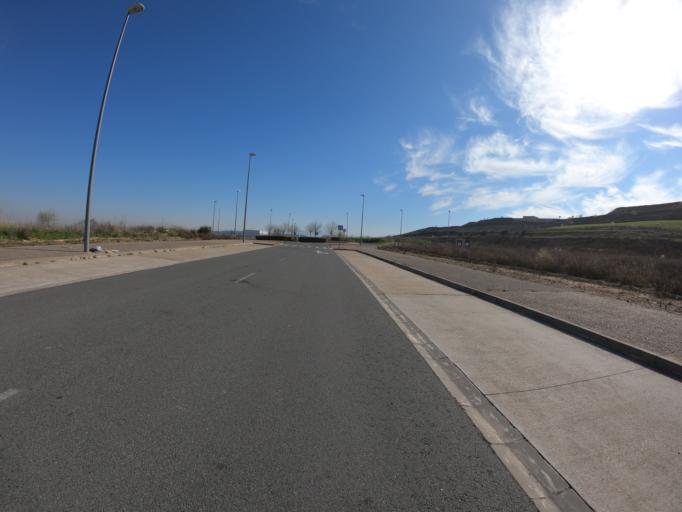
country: ES
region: Basque Country
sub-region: Provincia de Alava
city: Oyon
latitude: 42.4818
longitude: -2.4230
